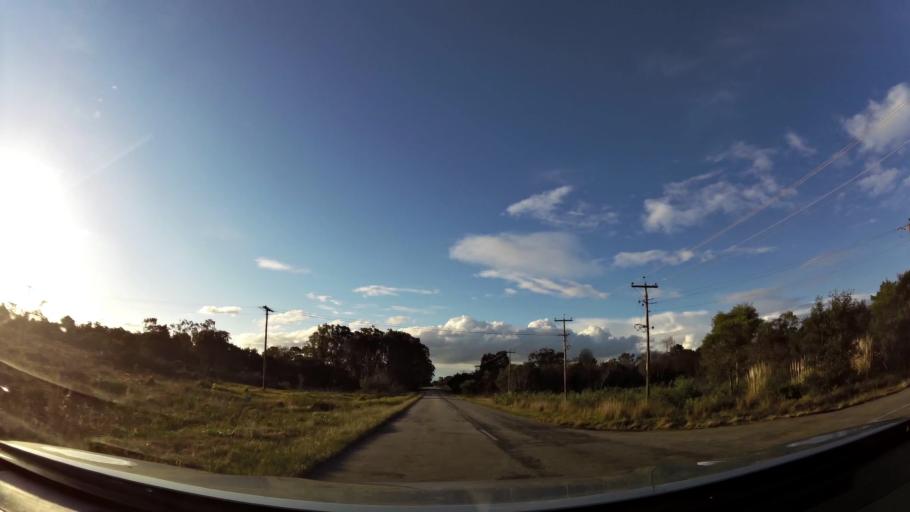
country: ZA
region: Eastern Cape
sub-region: Nelson Mandela Bay Metropolitan Municipality
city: Port Elizabeth
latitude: -33.9827
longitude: 25.4840
